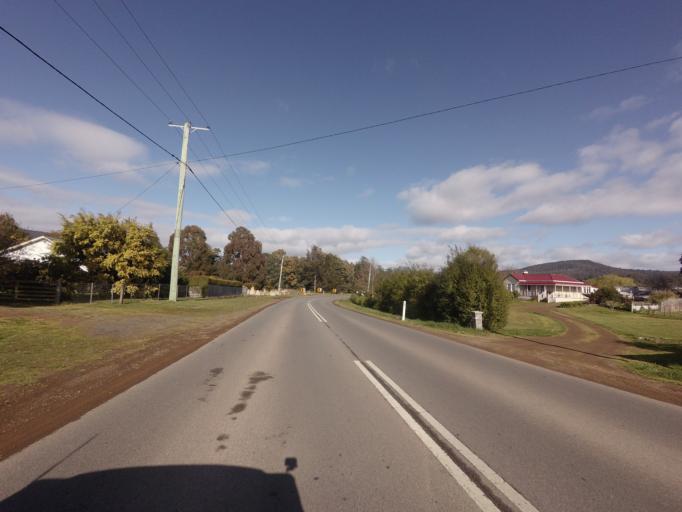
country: AU
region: Tasmania
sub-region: Huon Valley
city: Geeveston
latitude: -43.3219
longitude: 147.0035
